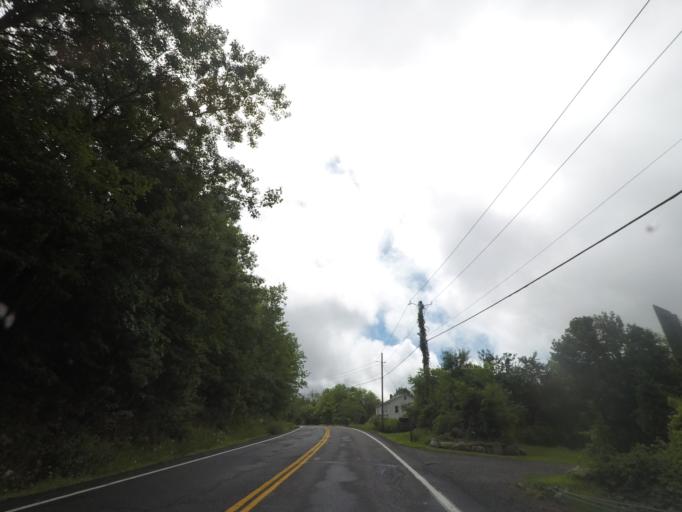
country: US
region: New York
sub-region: Rensselaer County
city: Averill Park
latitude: 42.5741
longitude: -73.4678
